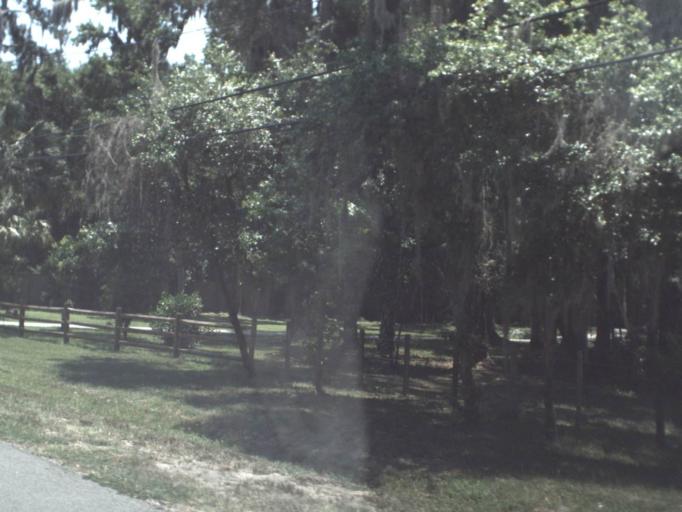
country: US
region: Florida
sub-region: Clay County
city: Green Cove Springs
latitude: 30.0390
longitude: -81.6670
